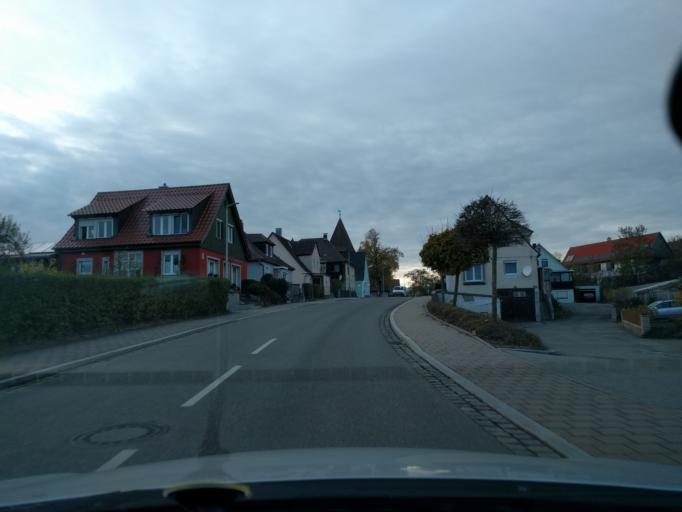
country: DE
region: Bavaria
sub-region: Regierungsbezirk Mittelfranken
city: Herrieden
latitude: 49.2358
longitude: 10.4942
